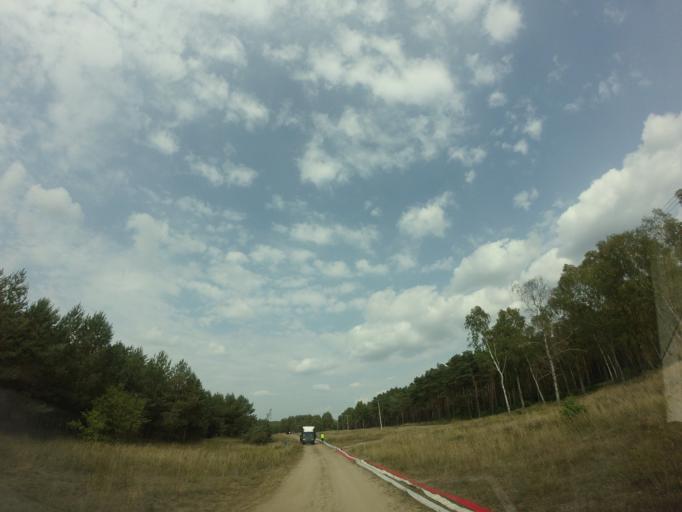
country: PL
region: West Pomeranian Voivodeship
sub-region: Powiat drawski
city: Drawsko Pomorskie
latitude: 53.4669
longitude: 15.7134
